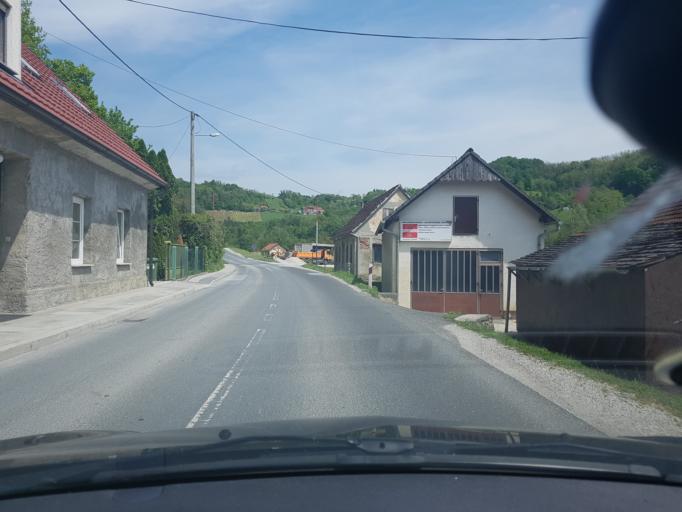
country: HR
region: Krapinsko-Zagorska
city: Pregrada
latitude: 46.1683
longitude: 15.7523
